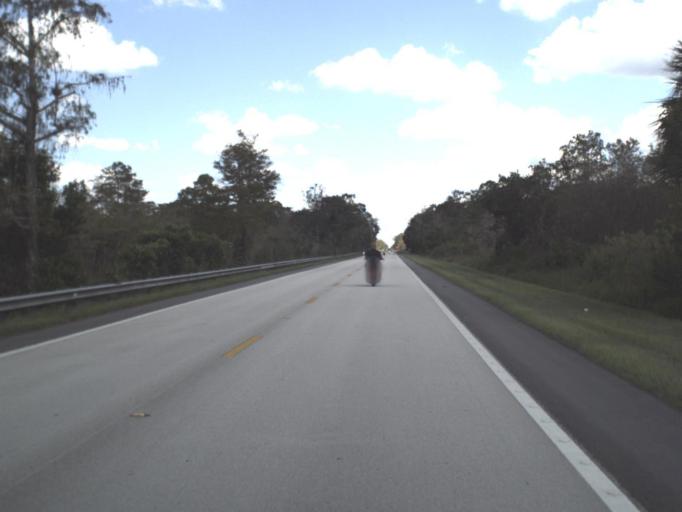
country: US
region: Florida
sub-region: Collier County
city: Lely Resort
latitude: 25.8700
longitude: -81.1621
